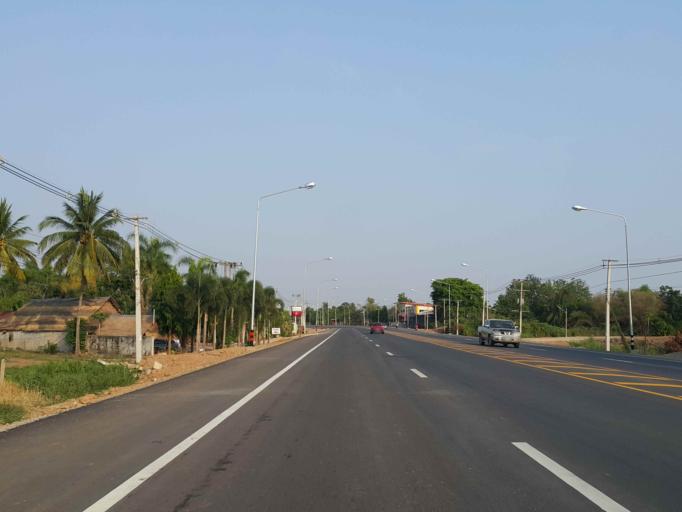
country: TH
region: Sukhothai
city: Sawankhalok
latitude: 17.3046
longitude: 99.8219
